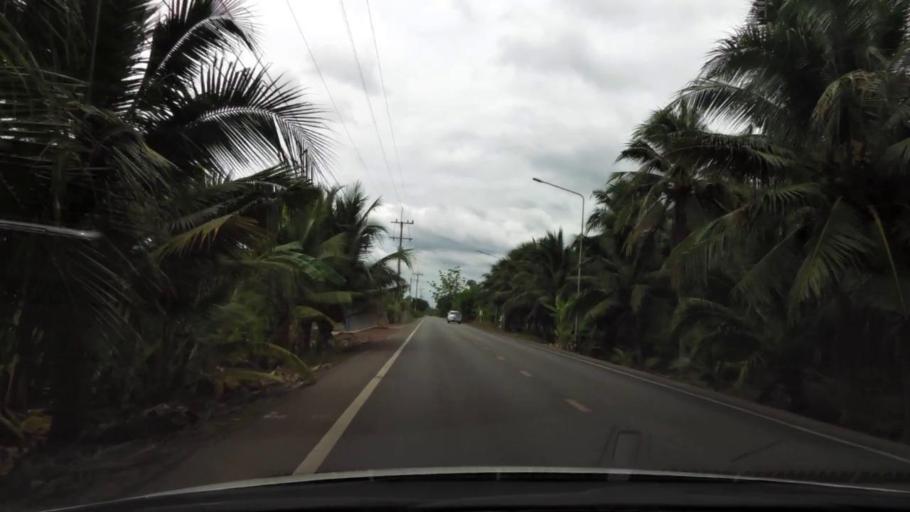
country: TH
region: Ratchaburi
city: Damnoen Saduak
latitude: 13.5630
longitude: 100.0128
